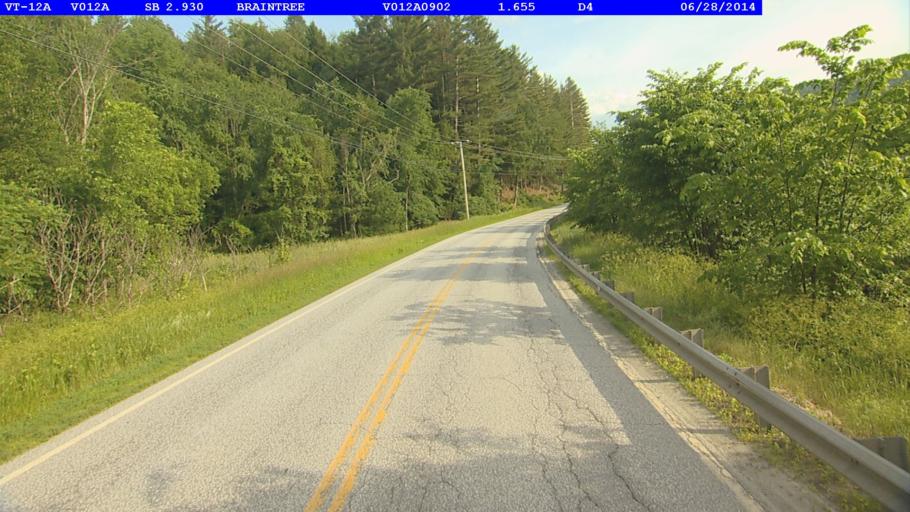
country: US
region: Vermont
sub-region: Orange County
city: Randolph
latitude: 43.9451
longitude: -72.7086
